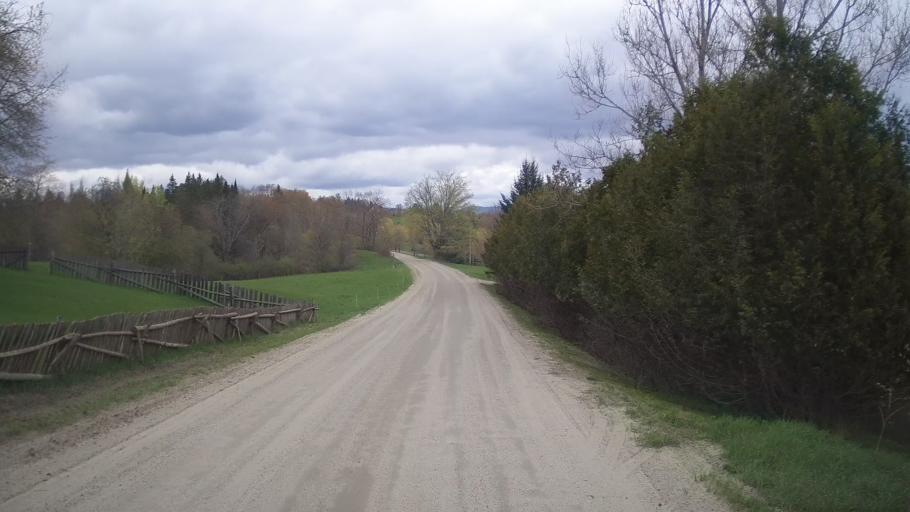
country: US
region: Vermont
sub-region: Caledonia County
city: Lyndonville
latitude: 44.6012
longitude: -71.9528
